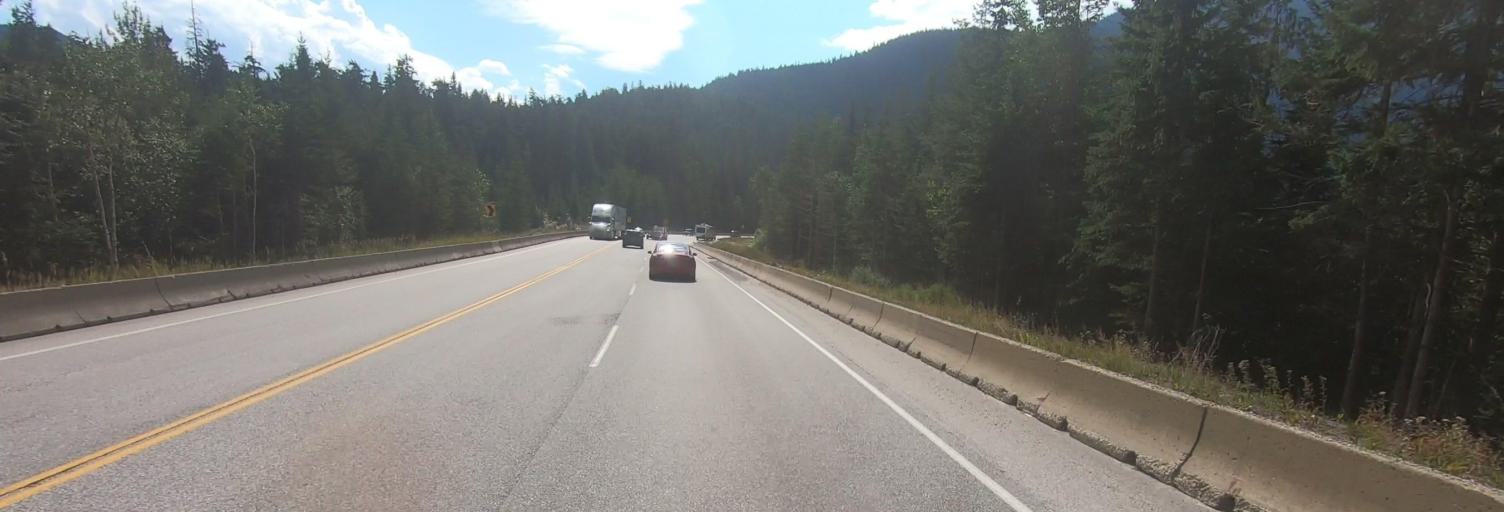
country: CA
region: British Columbia
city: Golden
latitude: 51.3478
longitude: -117.4355
